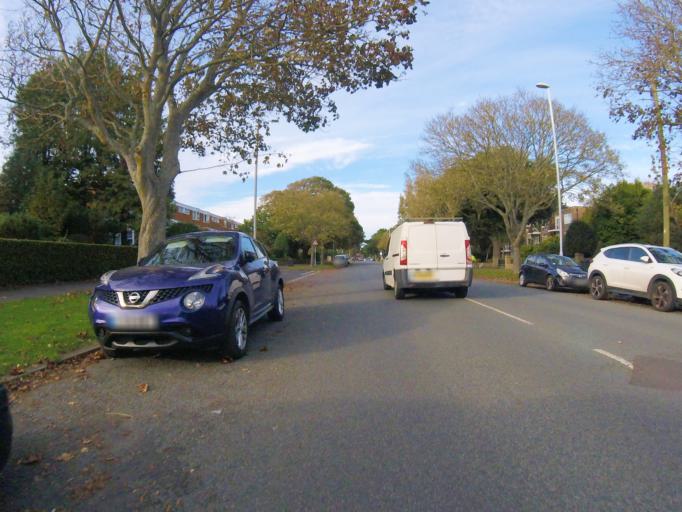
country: GB
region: England
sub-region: West Sussex
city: Worthing
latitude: 50.8117
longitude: -0.3932
